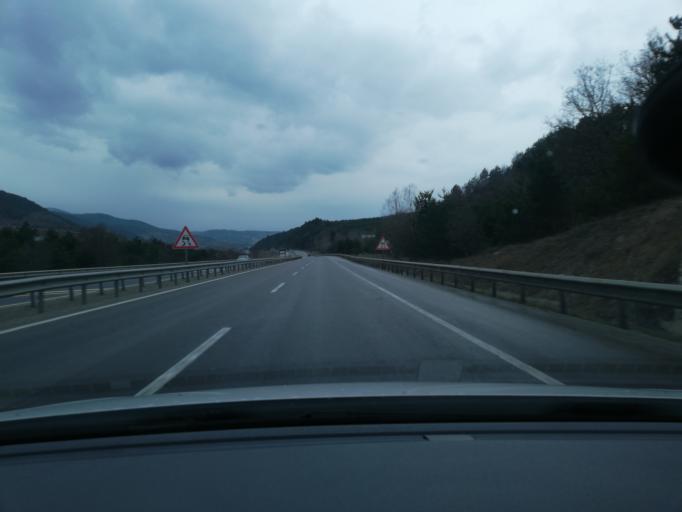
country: TR
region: Bolu
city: Yenicaga
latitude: 40.7490
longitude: 31.8897
